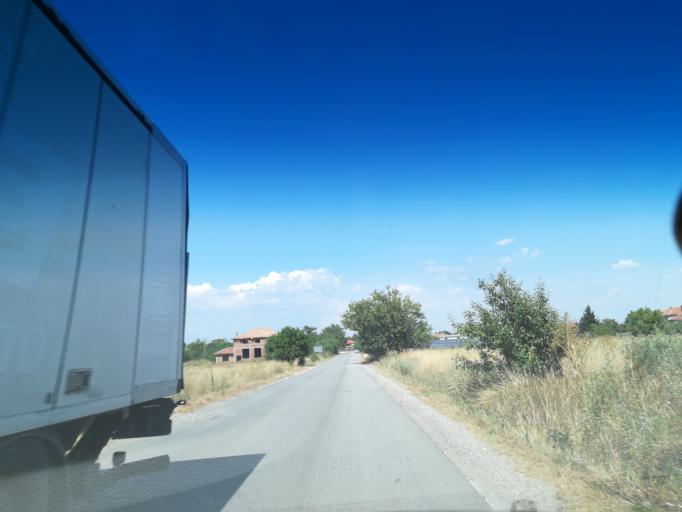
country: BG
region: Stara Zagora
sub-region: Obshtina Chirpan
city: Chirpan
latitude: 42.0730
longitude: 25.1859
